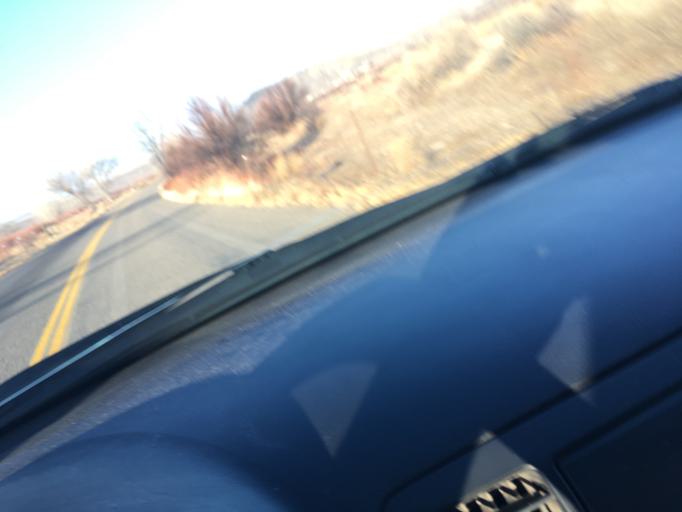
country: US
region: Colorado
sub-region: Delta County
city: Delta
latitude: 38.7475
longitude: -108.1422
